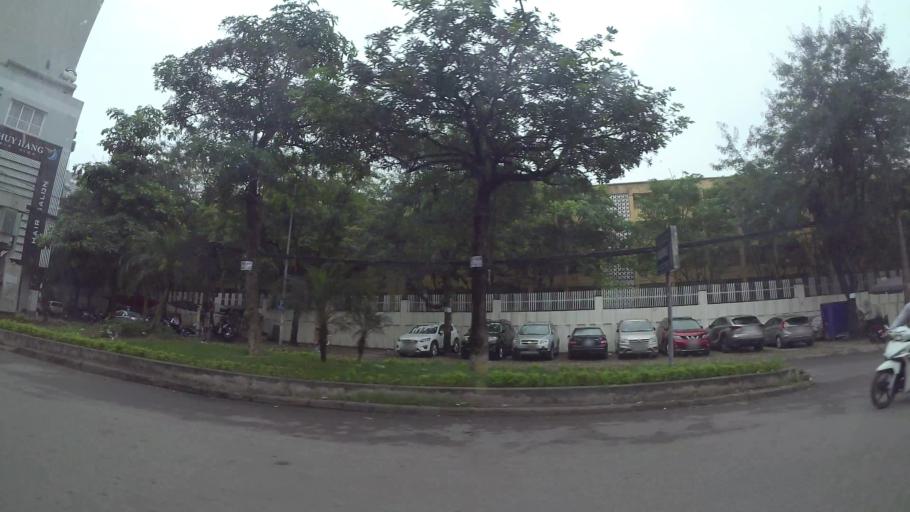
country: VN
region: Ha Noi
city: Dong Da
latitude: 21.0125
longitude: 105.8324
